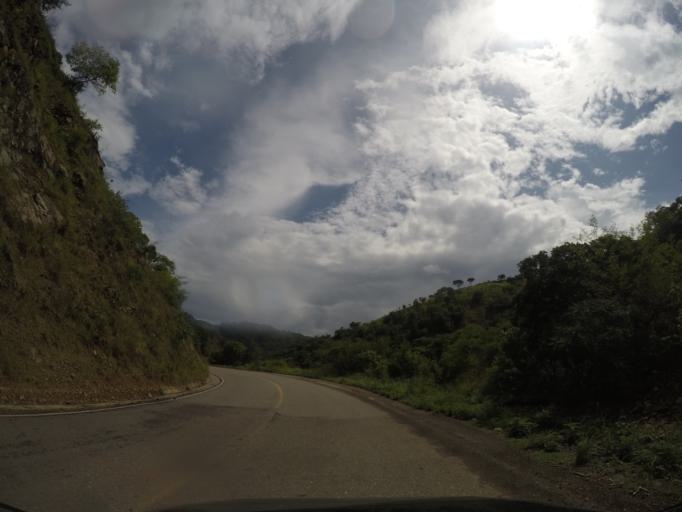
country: MX
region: Oaxaca
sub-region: San Jeronimo Coatlan
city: San Cristobal Honduras
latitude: 16.3817
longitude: -97.0766
